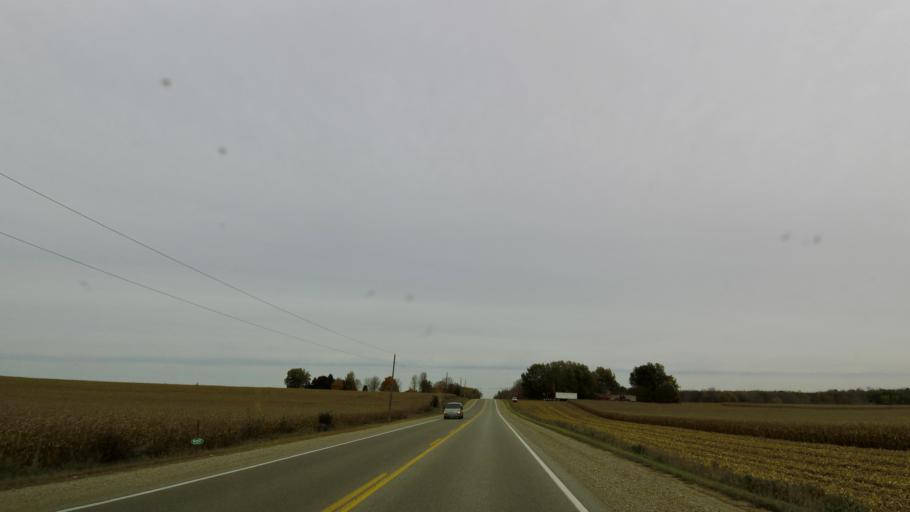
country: CA
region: Ontario
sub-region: Wellington County
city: Guelph
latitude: 43.5092
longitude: -80.3061
